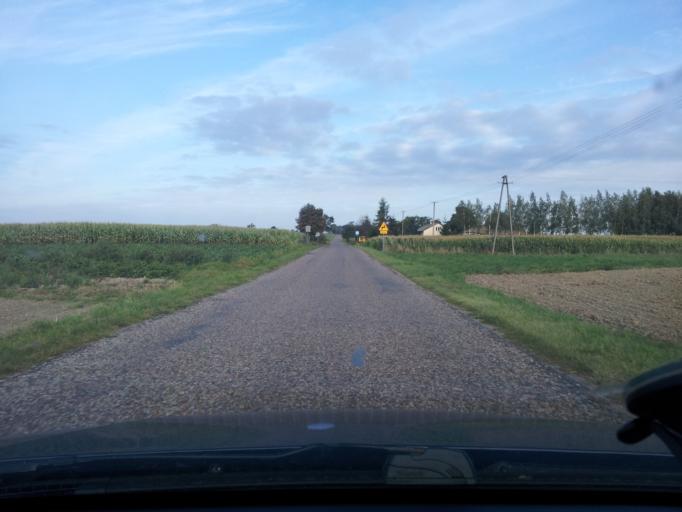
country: PL
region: Kujawsko-Pomorskie
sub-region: Powiat brodnicki
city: Gorzno
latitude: 53.2034
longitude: 19.5990
